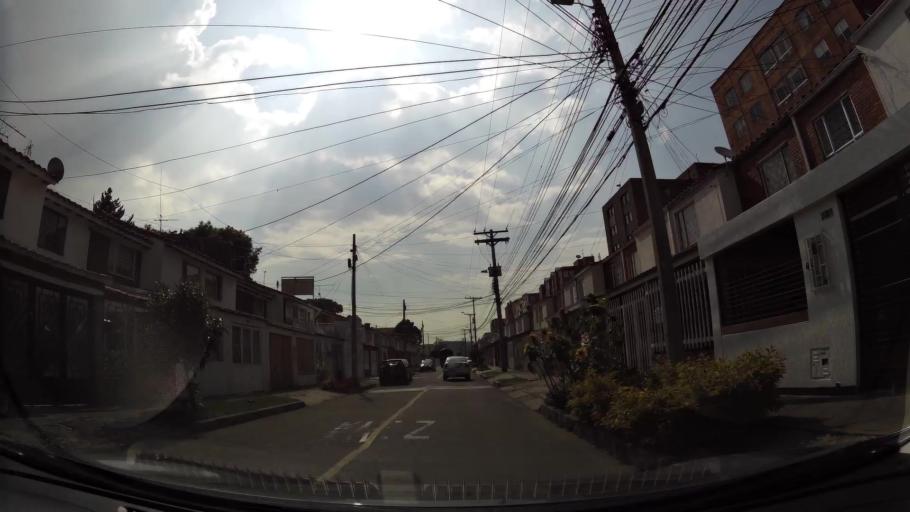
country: CO
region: Bogota D.C.
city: Barrio San Luis
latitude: 4.7310
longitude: -74.0521
